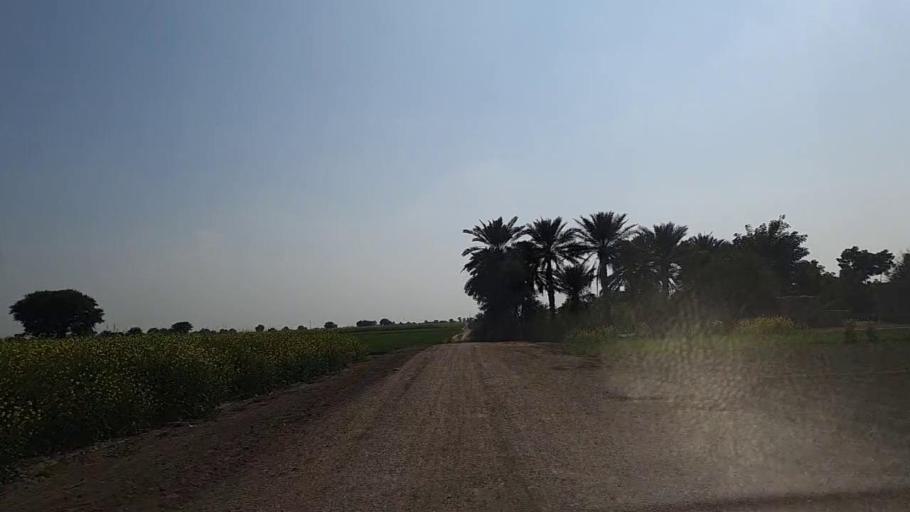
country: PK
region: Sindh
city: Jam Sahib
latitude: 26.2431
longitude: 68.5667
